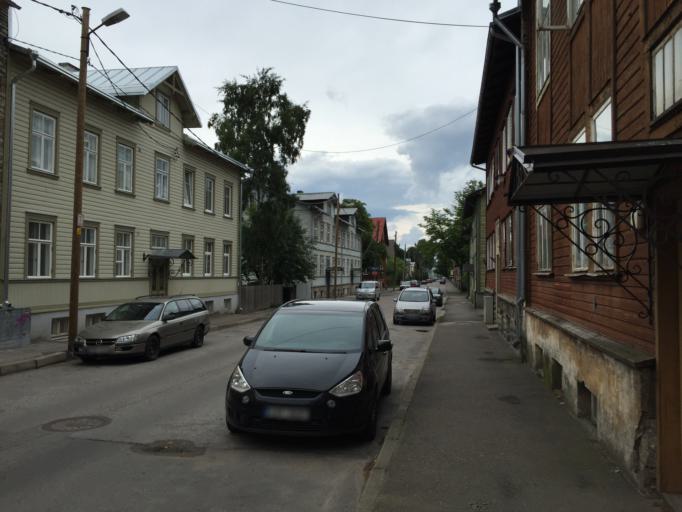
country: EE
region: Harju
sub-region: Tallinna linn
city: Tallinn
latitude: 59.4442
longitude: 24.7239
